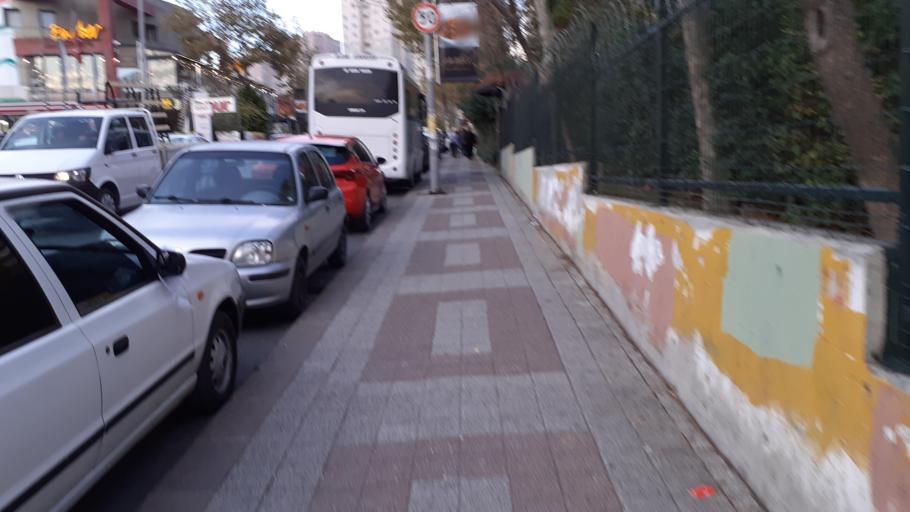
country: TR
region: Istanbul
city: Mahmutbey
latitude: 41.0559
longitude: 28.7902
